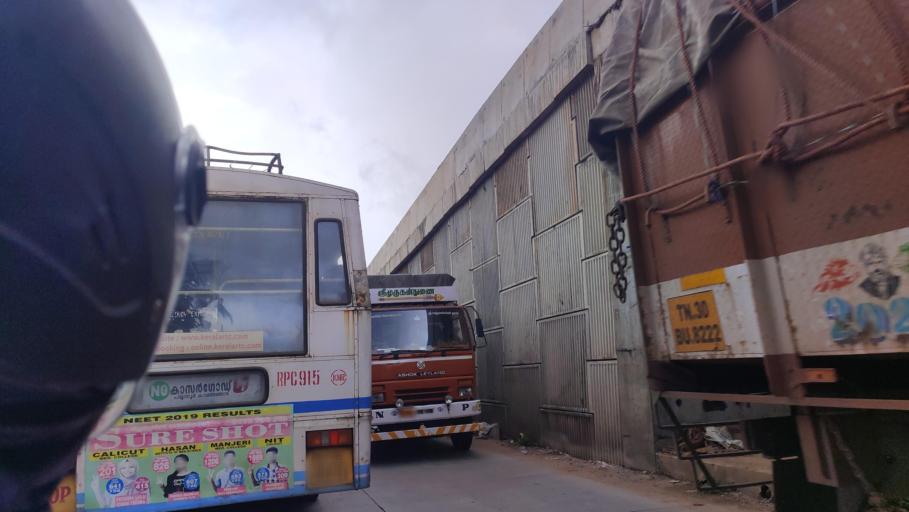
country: IN
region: Kerala
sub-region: Kasaragod District
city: Nileshwar
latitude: 12.2430
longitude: 75.1439
